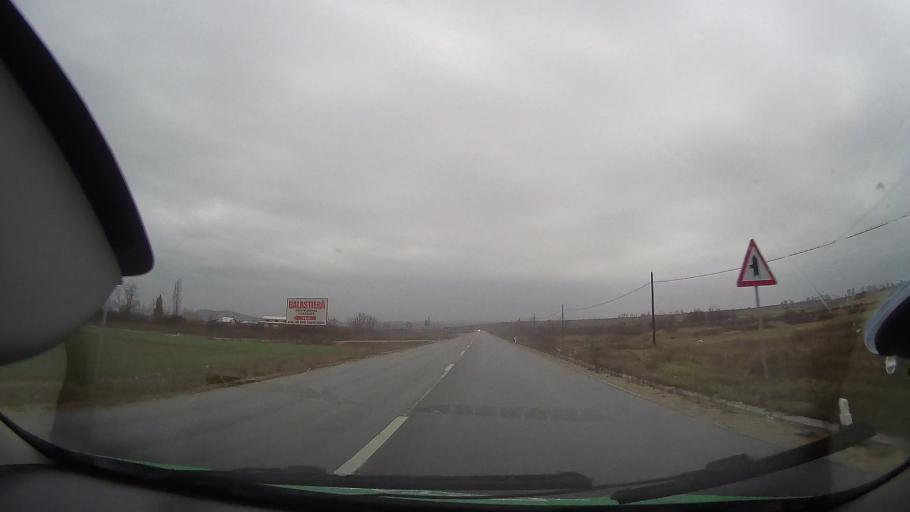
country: RO
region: Bihor
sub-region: Municipiul Beius
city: Beius
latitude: 46.6759
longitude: 22.3224
